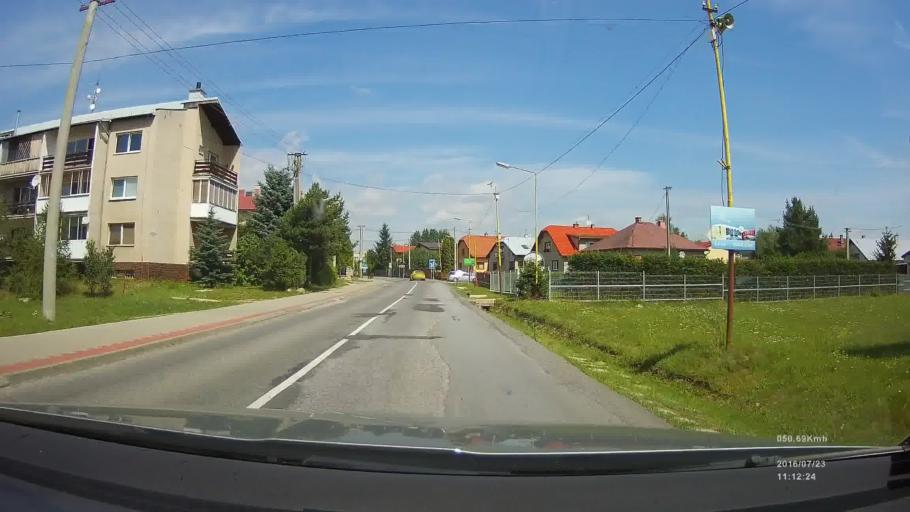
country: SK
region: Presovsky
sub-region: Okres Poprad
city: Poprad
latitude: 49.1175
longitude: 20.3537
